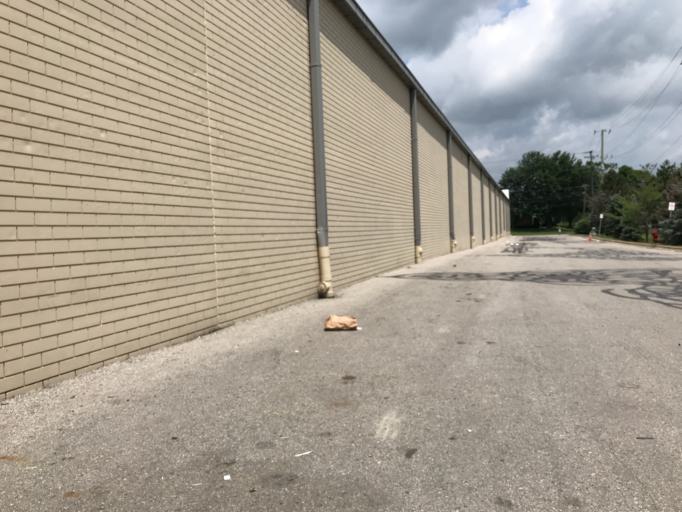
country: US
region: Michigan
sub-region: Oakland County
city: Bingham Farms
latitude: 42.5000
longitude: -83.2816
